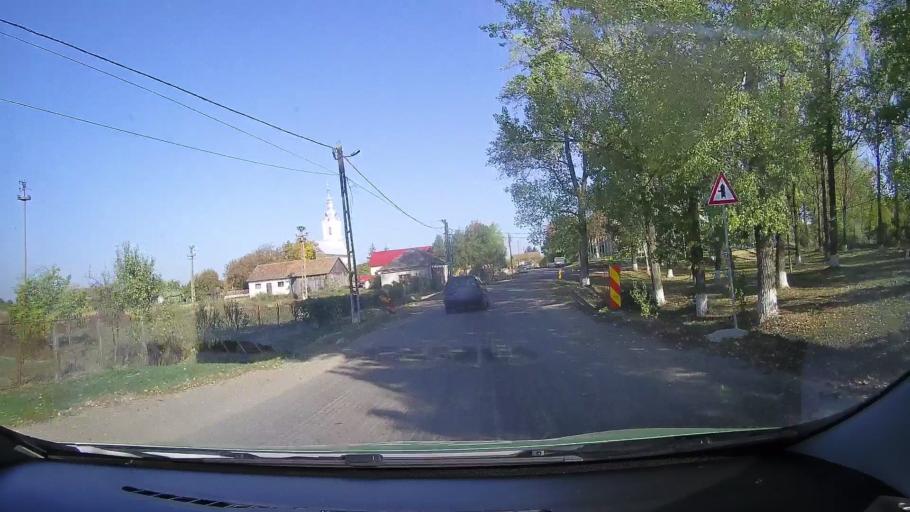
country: RO
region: Satu Mare
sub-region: Comuna Santau
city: Santau
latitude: 47.5084
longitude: 22.5075
